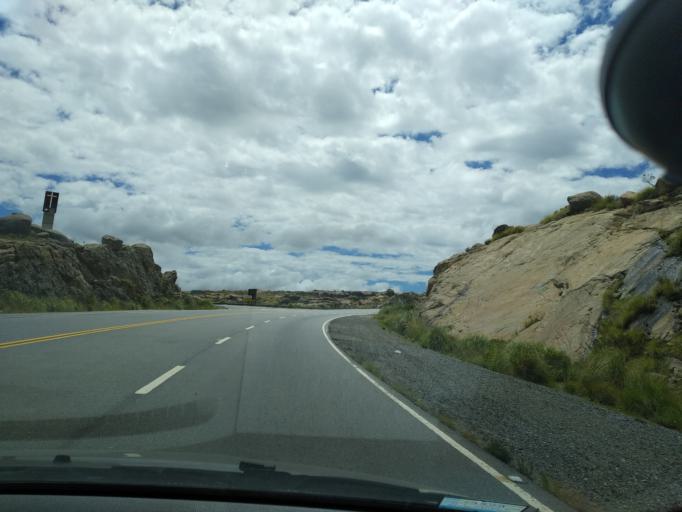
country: AR
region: Cordoba
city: Villa Cura Brochero
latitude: -31.6132
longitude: -64.9079
